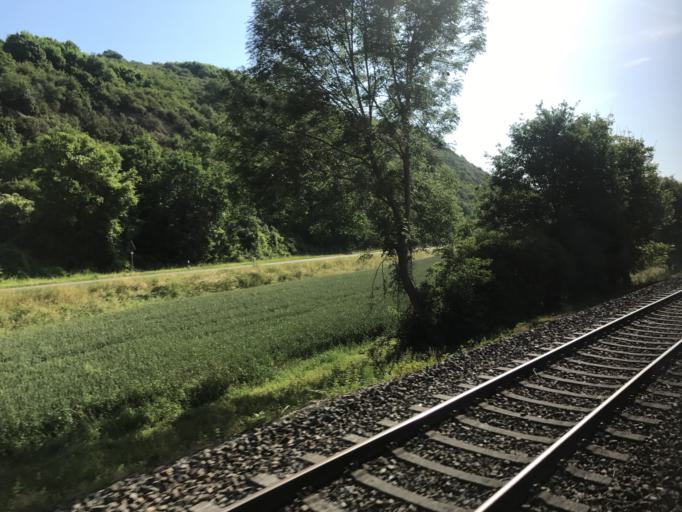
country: DE
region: Rheinland-Pfalz
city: Staudernheim
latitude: 49.7813
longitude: 7.6787
